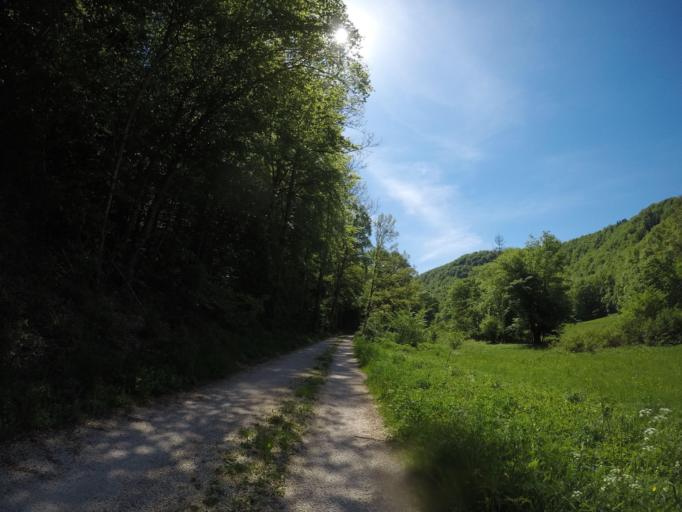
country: DE
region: Baden-Wuerttemberg
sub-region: Tuebingen Region
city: Blaubeuren
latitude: 48.3966
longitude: 9.7587
